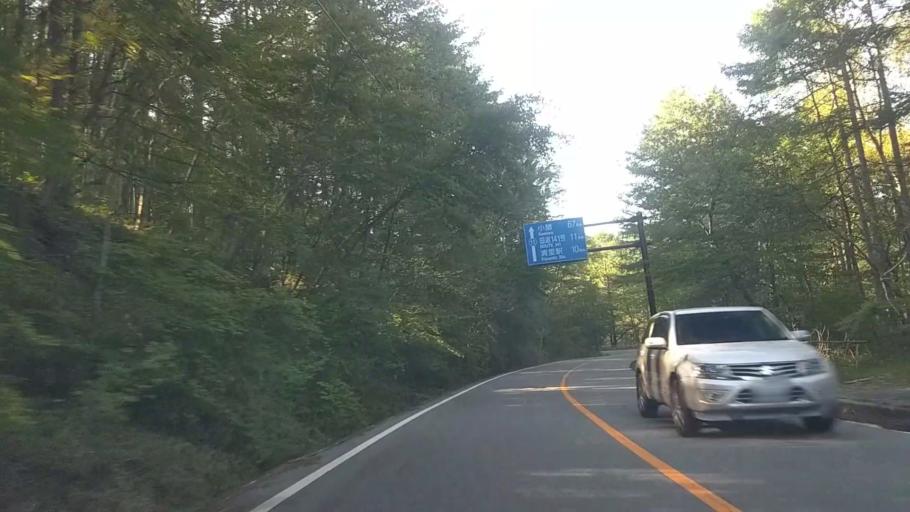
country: JP
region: Yamanashi
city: Nirasaki
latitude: 35.9034
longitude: 138.3854
